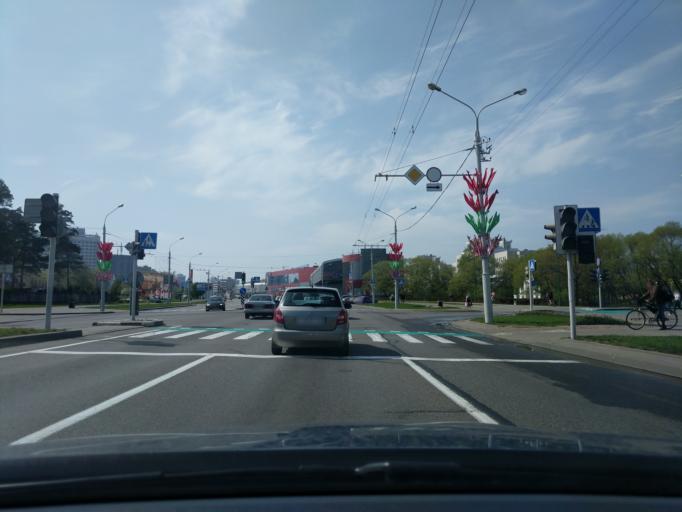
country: BY
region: Minsk
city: Novoye Medvezhino
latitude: 53.9366
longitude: 27.4945
